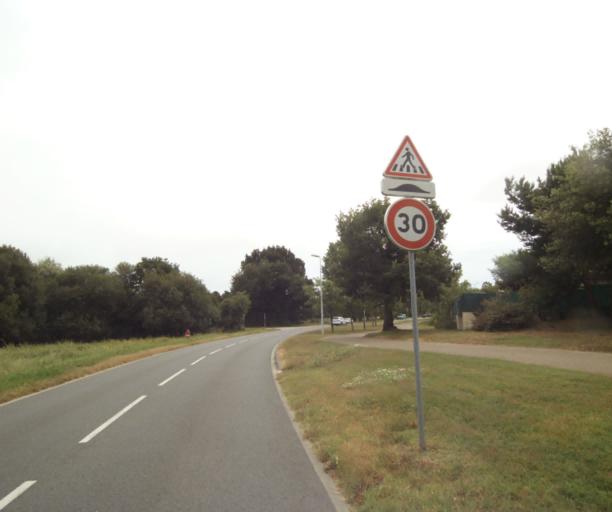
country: FR
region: Pays de la Loire
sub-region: Departement de la Vendee
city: Chateau-d'Olonne
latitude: 46.4985
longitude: -1.7408
